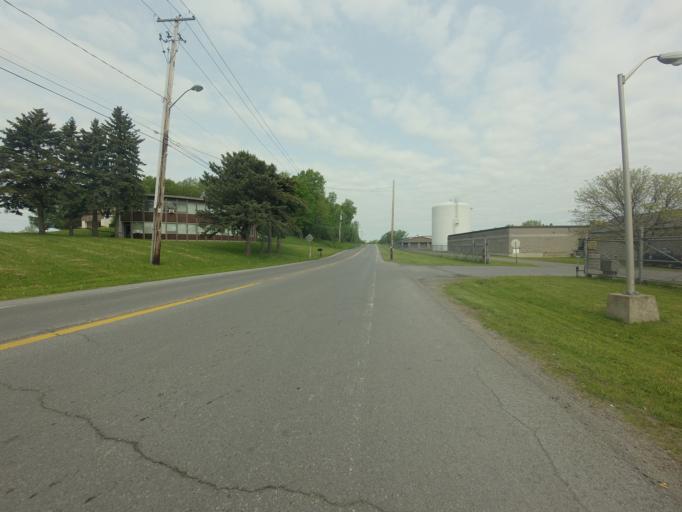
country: US
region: New York
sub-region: Jefferson County
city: Watertown
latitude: 43.9752
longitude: -75.8755
